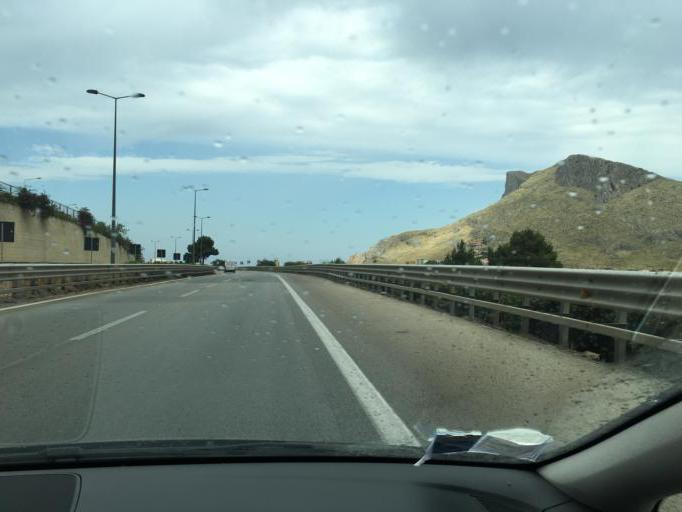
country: IT
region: Sicily
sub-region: Palermo
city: Isola delle Femmine
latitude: 38.1839
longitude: 13.2903
